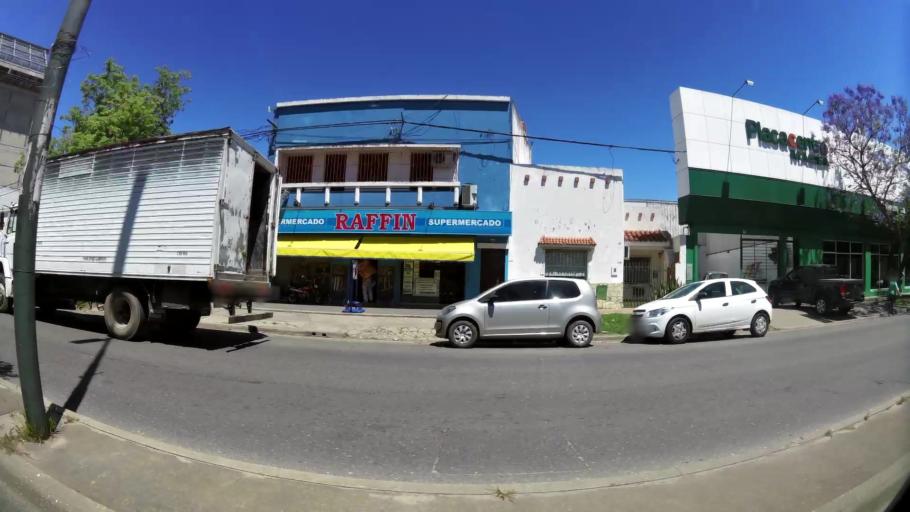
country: AR
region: Santa Fe
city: Santa Fe de la Vera Cruz
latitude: -31.6230
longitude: -60.7053
